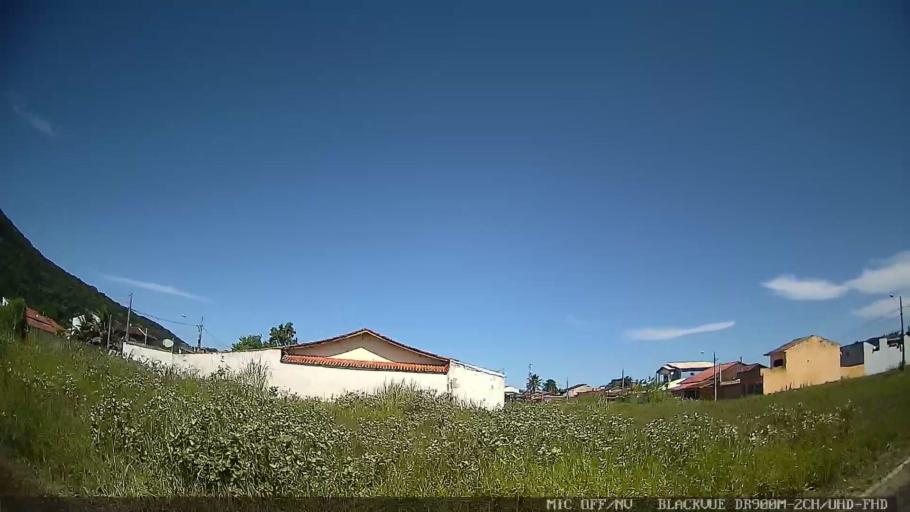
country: BR
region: Sao Paulo
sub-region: Iguape
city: Iguape
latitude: -24.6943
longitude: -47.5626
